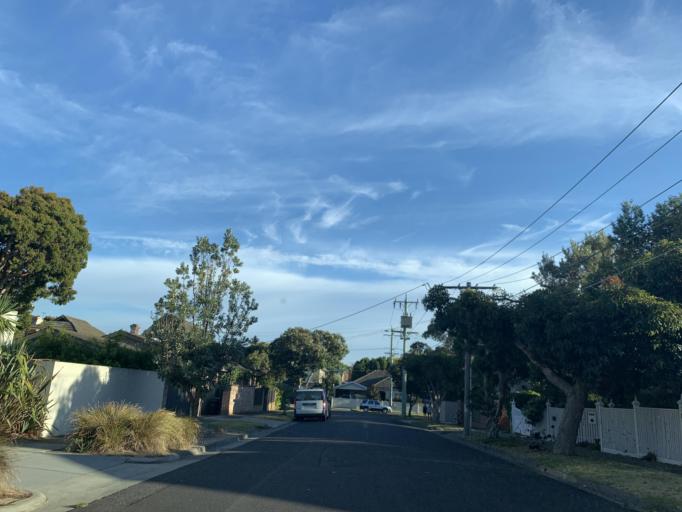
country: AU
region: Victoria
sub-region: Bayside
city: Black Rock
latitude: -37.9631
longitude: 145.0137
